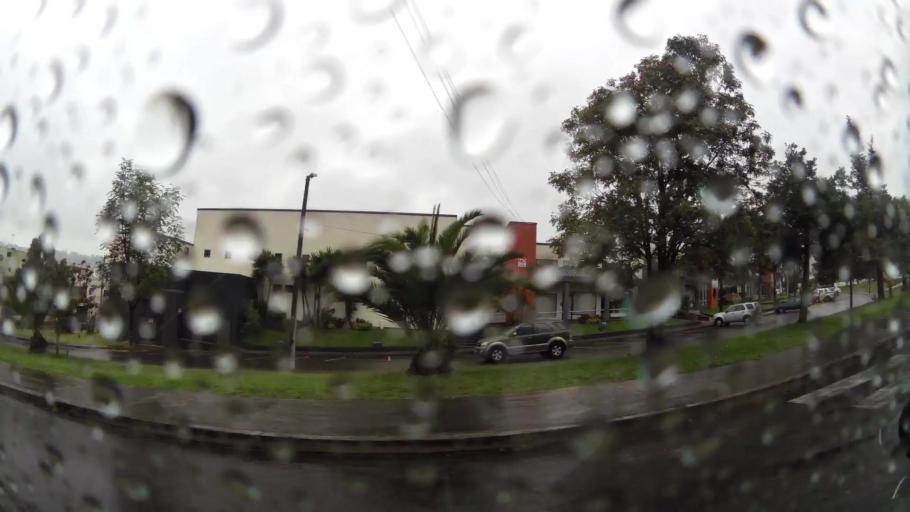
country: EC
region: Pichincha
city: Quito
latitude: -0.1026
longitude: -78.4999
